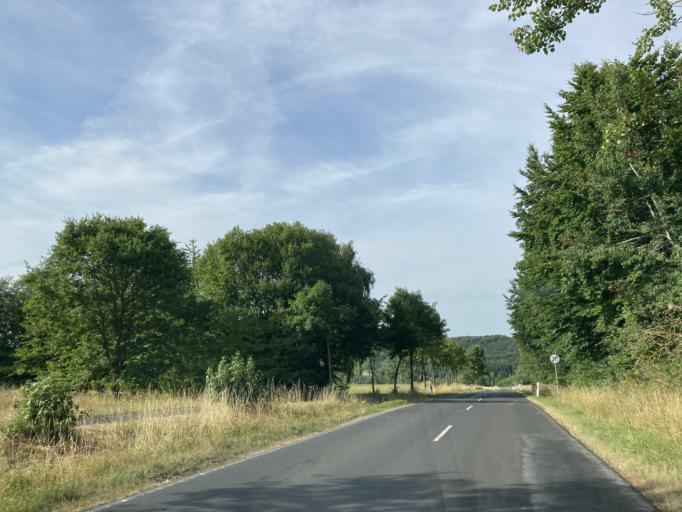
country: DE
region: Hesse
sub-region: Regierungsbezirk Kassel
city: Hosenfeld
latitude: 50.4797
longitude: 9.4755
